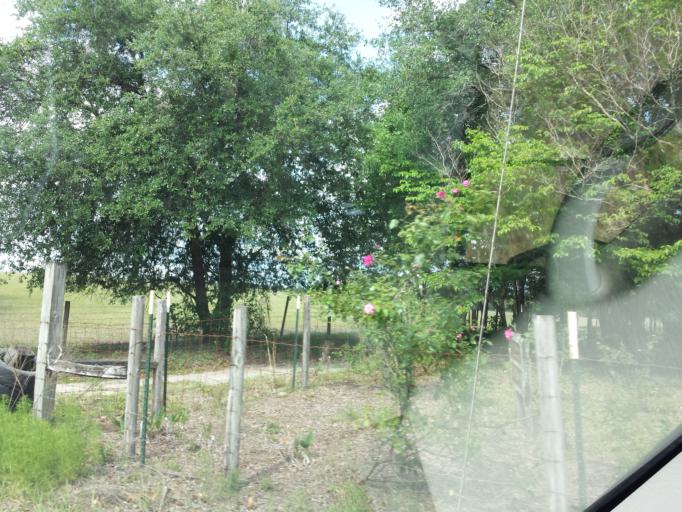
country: US
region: Florida
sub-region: Hernando County
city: Hill 'n Dale
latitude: 28.5353
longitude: -82.2842
